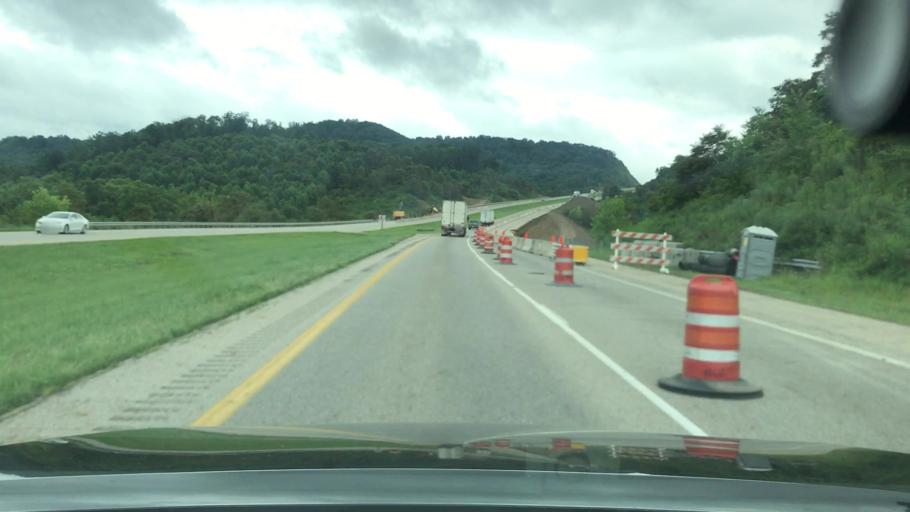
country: US
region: Ohio
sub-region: Ross County
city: Chillicothe
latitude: 39.2427
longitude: -82.8429
